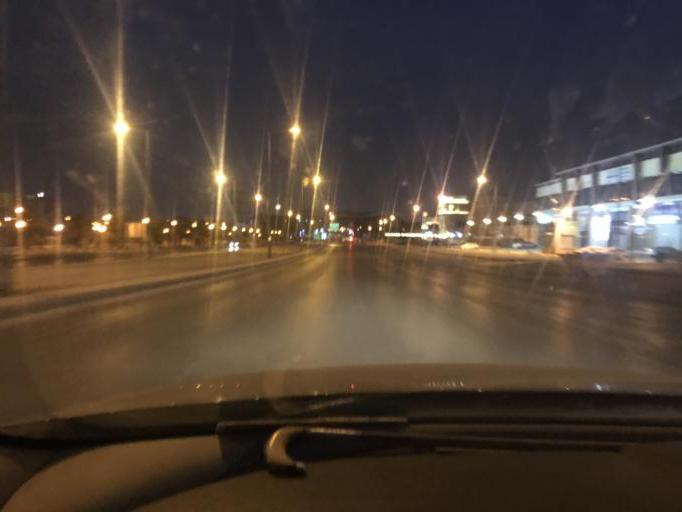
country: SA
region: Ar Riyad
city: Riyadh
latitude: 24.8053
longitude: 46.6939
